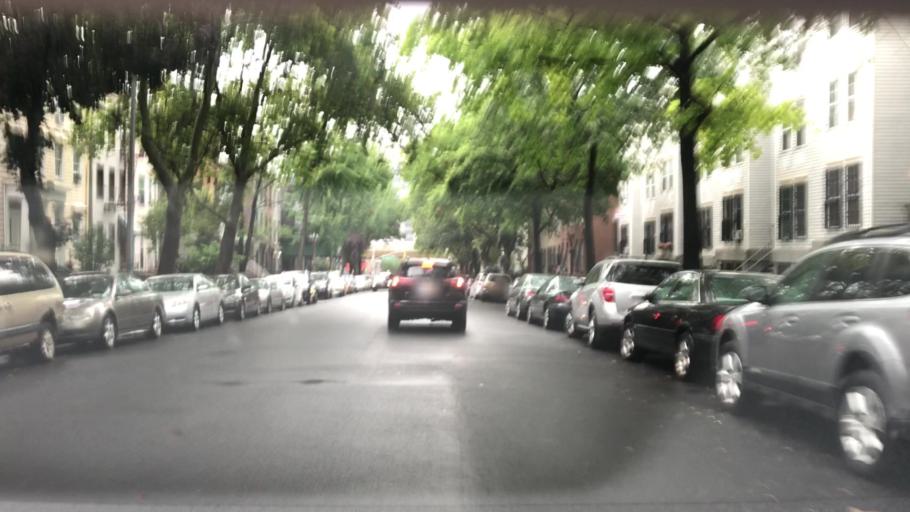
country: US
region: New York
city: New York City
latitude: 40.6944
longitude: -73.9701
